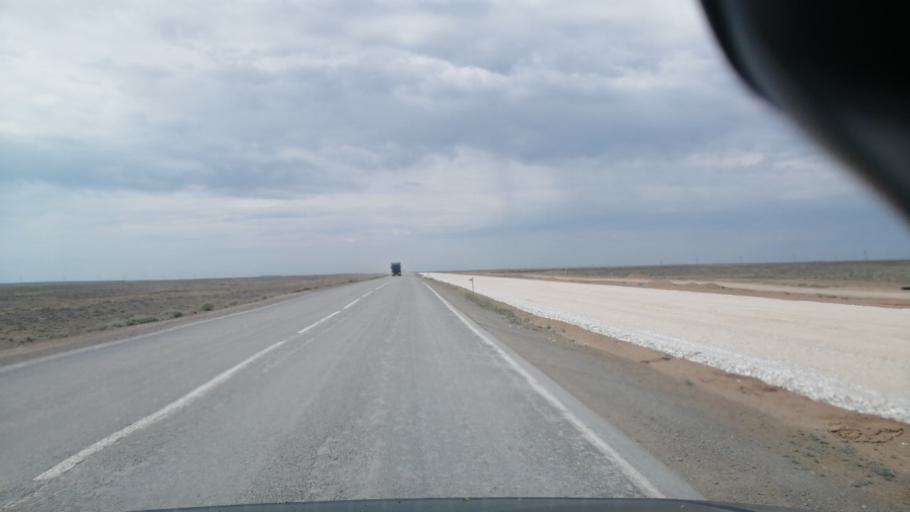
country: KZ
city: Priozersk
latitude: 46.5823
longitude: 74.2479
